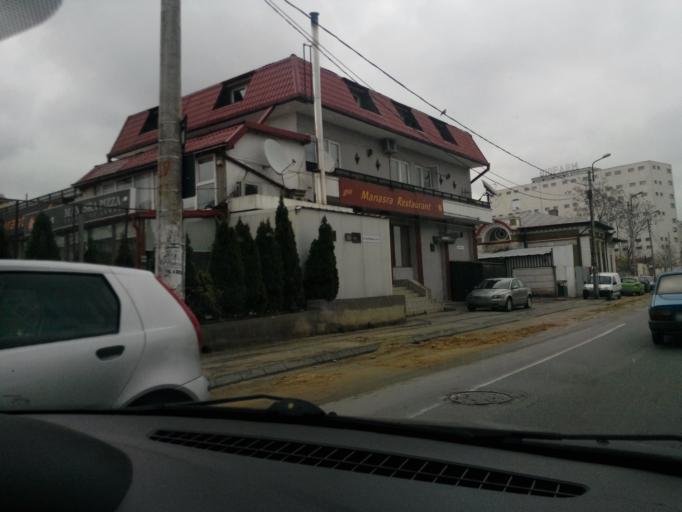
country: RO
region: Bucuresti
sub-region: Municipiul Bucuresti
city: Bucharest
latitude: 44.4178
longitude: 26.1144
